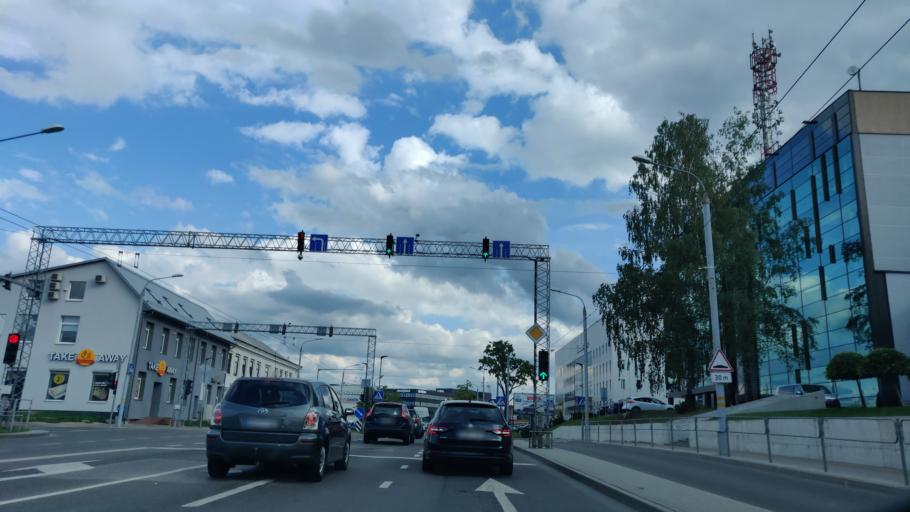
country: LT
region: Vilnius County
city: Vilkpede
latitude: 54.6722
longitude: 25.2561
